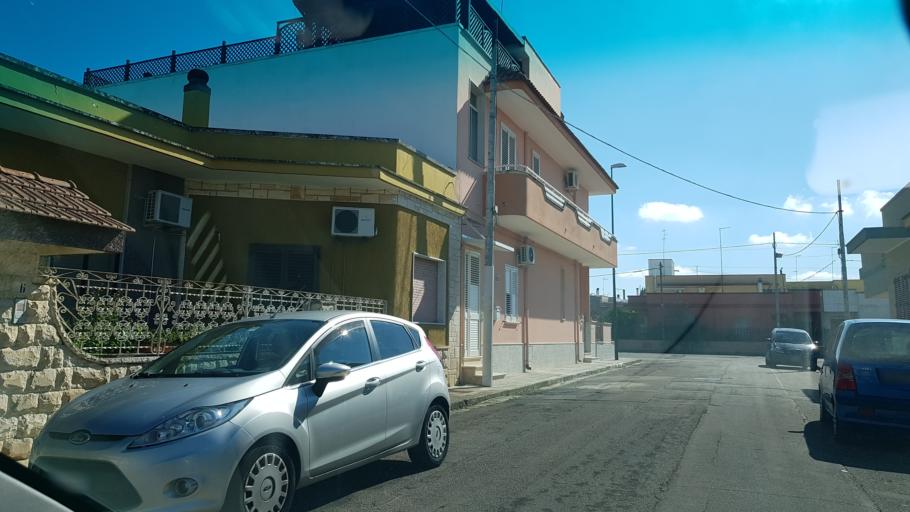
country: IT
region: Apulia
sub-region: Provincia di Lecce
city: Campi Salentina
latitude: 40.3942
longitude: 18.0095
